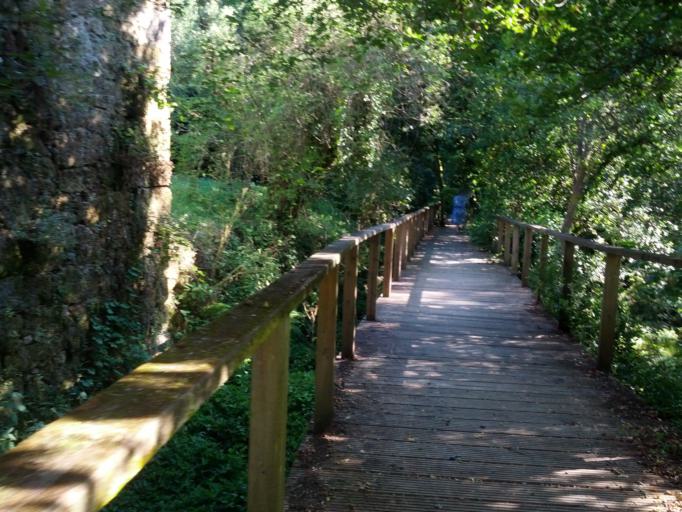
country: ES
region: Galicia
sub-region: Provincia da Coruna
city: Santiago de Compostela
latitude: 42.8762
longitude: -8.5637
